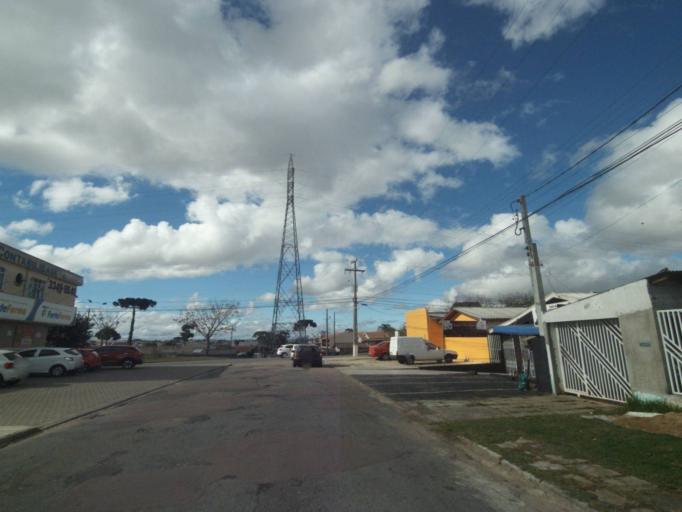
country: BR
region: Parana
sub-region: Sao Jose Dos Pinhais
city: Sao Jose dos Pinhais
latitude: -25.5295
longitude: -49.2906
